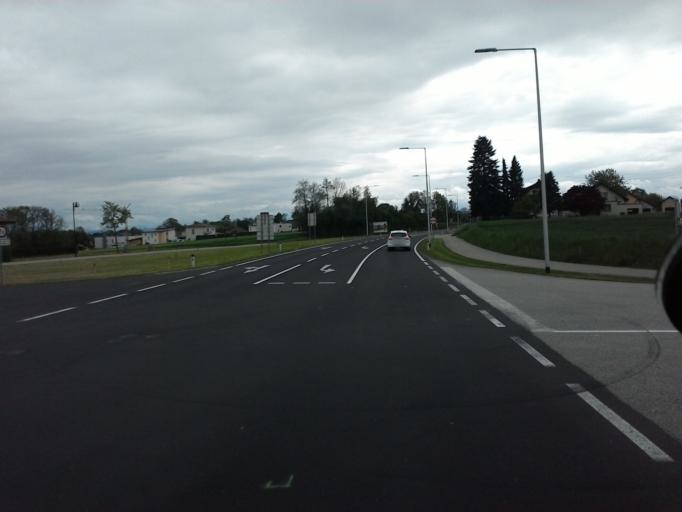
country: AT
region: Upper Austria
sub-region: Wels-Land
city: Sattledt
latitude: 48.0700
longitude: 14.0543
